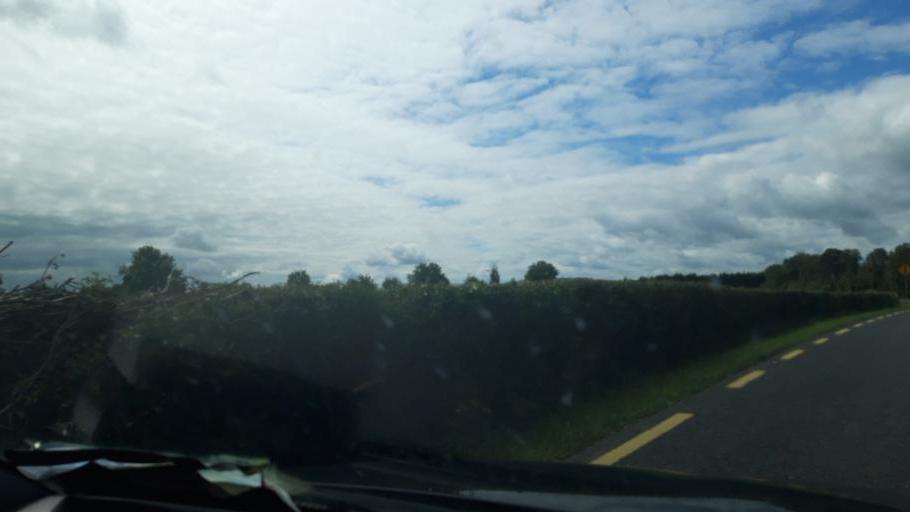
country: IE
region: Leinster
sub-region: Kilkenny
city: Callan
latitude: 52.5244
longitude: -7.4168
